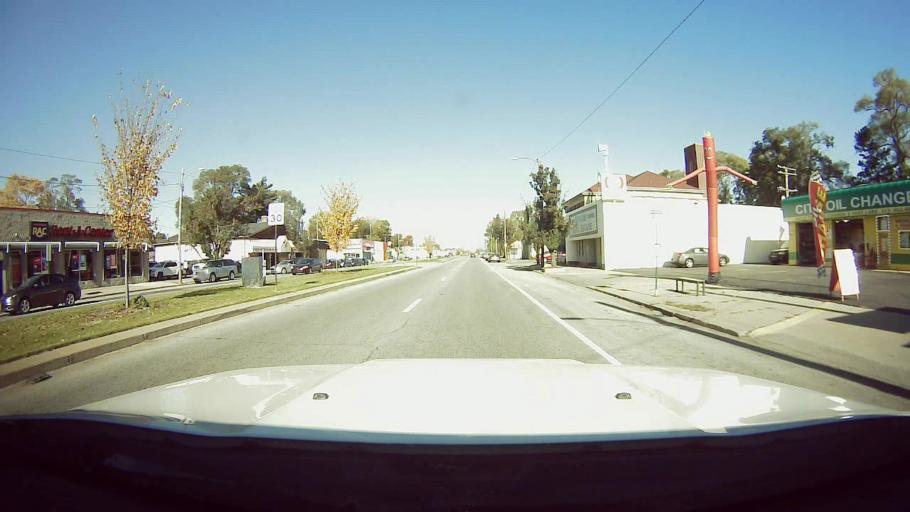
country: US
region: Michigan
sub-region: Oakland County
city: Ferndale
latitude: 42.4246
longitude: -83.1411
